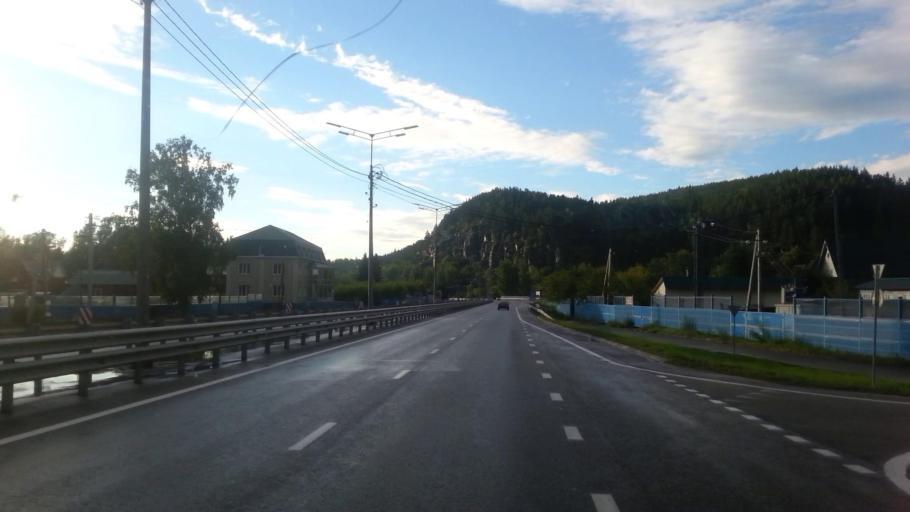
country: RU
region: Altay
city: Souzga
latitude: 51.9155
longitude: 85.8617
